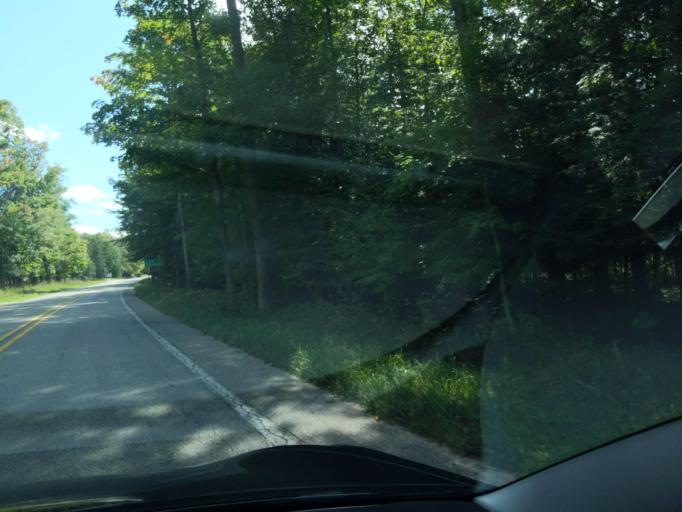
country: US
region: Michigan
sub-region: Antrim County
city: Bellaire
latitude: 45.0681
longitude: -85.3175
